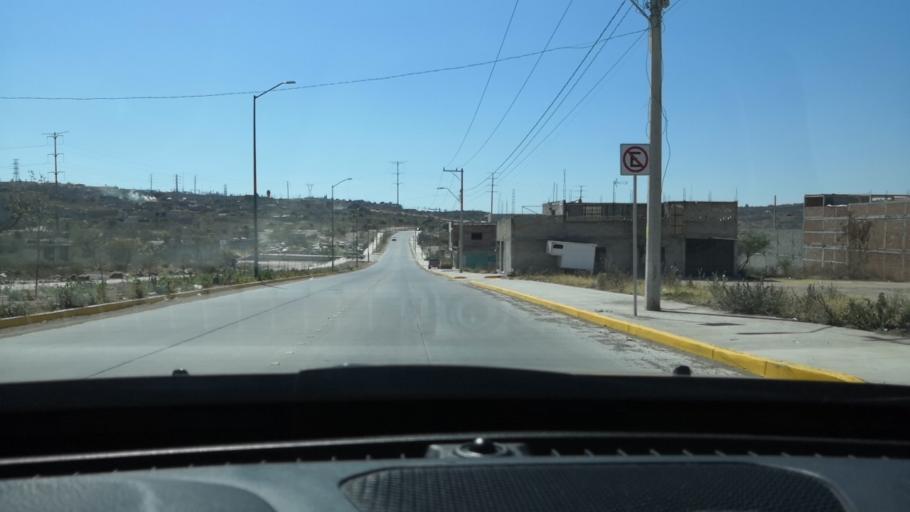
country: MX
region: Guanajuato
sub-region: Leon
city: Ejido la Joya
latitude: 21.1322
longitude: -101.7348
